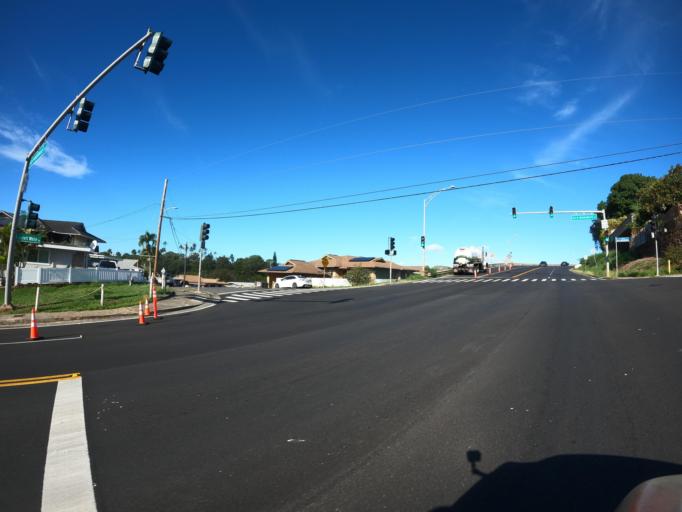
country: US
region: Hawaii
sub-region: Honolulu County
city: Halawa Heights
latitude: 21.3537
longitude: -157.8940
